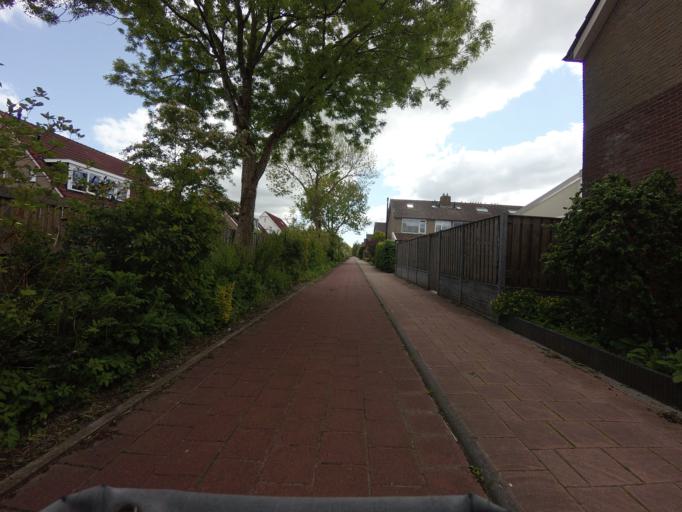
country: NL
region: Friesland
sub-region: Sudwest Fryslan
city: Bolsward
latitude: 53.0703
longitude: 5.5321
